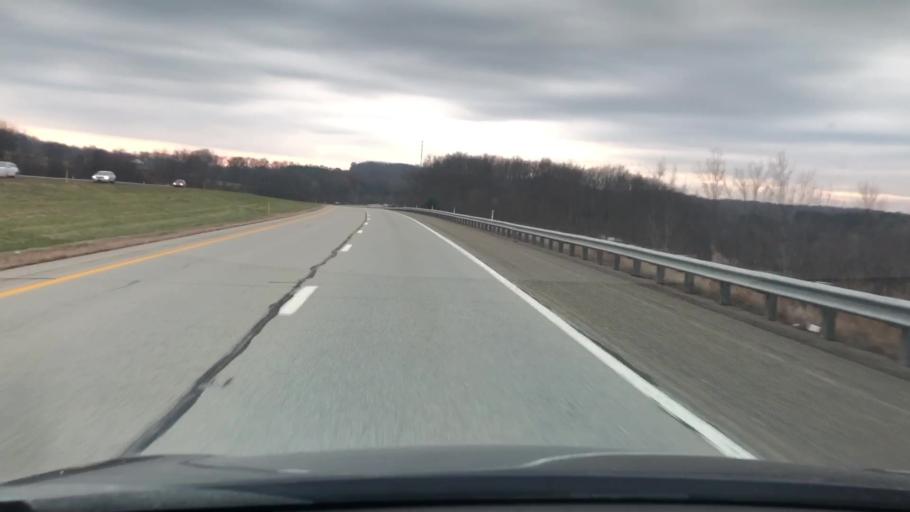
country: US
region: Pennsylvania
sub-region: Armstrong County
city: Freeport
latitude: 40.7307
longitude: -79.6665
